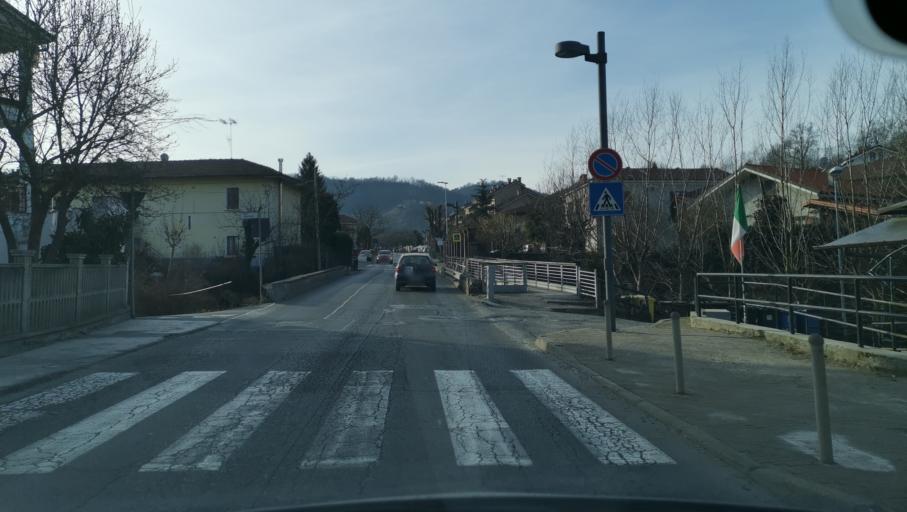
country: IT
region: Piedmont
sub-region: Provincia di Torino
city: Castiglione Torinese
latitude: 45.1129
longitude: 7.8164
